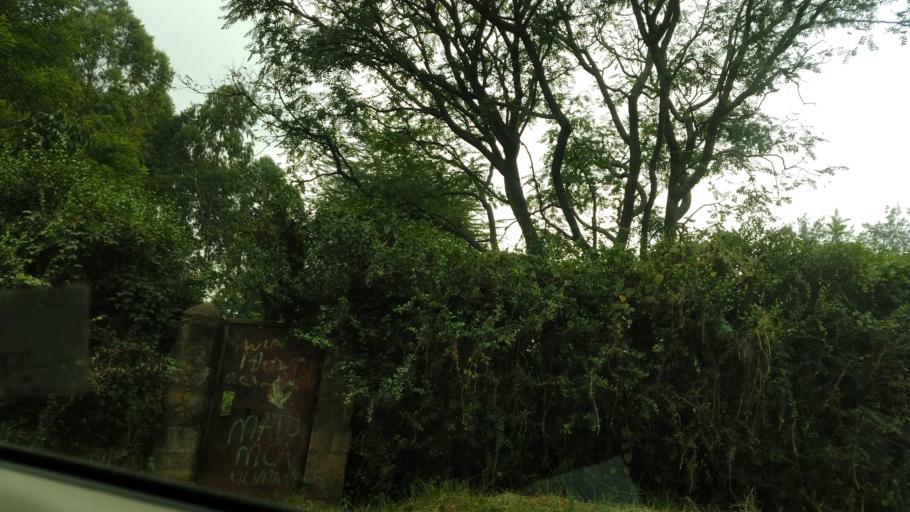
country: KE
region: Nairobi Area
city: Nairobi
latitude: -1.2945
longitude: 36.7818
